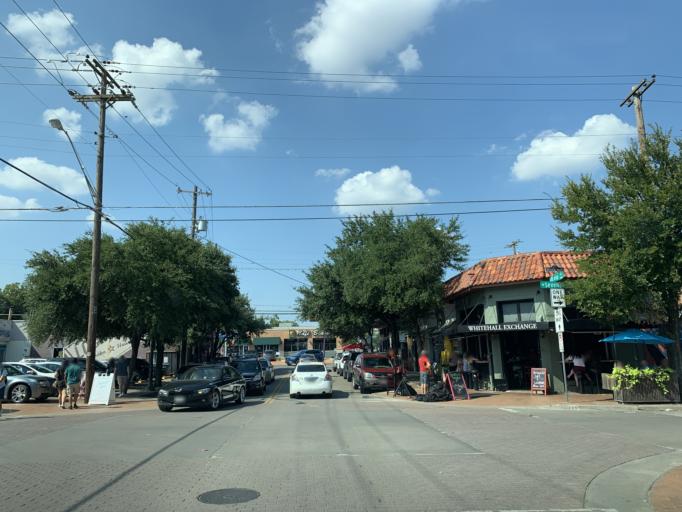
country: US
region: Texas
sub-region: Dallas County
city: Dallas
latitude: 32.7489
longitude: -96.8283
